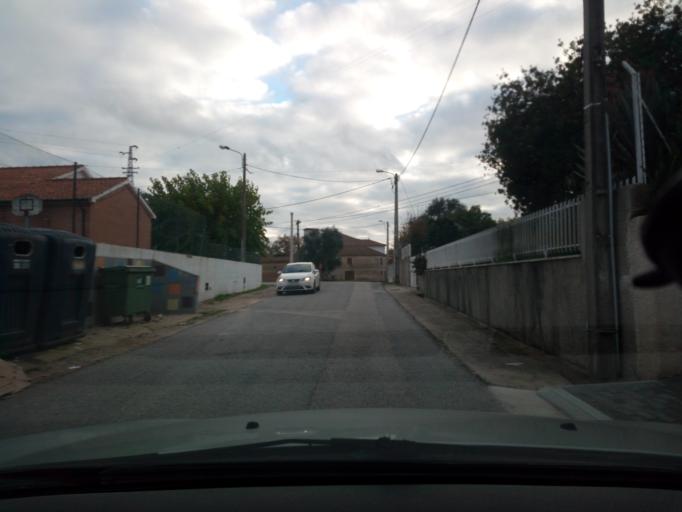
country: PT
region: Aveiro
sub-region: Oliveira do Bairro
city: Oliveira do Bairro
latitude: 40.5492
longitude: -8.4881
